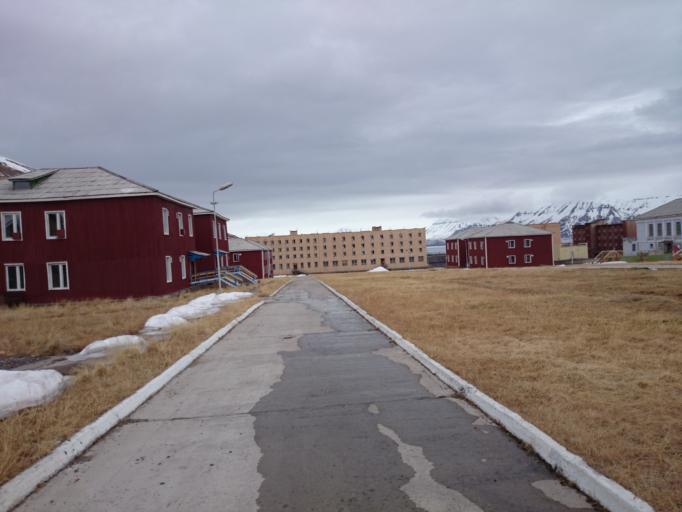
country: SJ
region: Svalbard
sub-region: Spitsbergen
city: Longyearbyen
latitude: 78.6559
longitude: 16.3171
